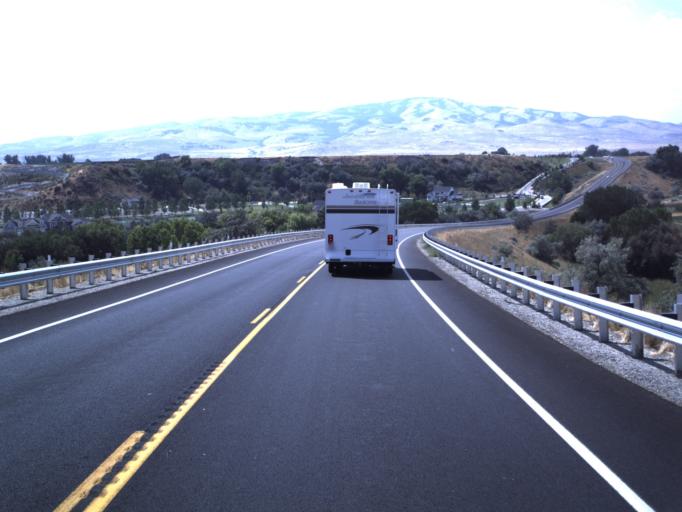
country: US
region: Utah
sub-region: Box Elder County
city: Garland
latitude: 41.7834
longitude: -112.1057
